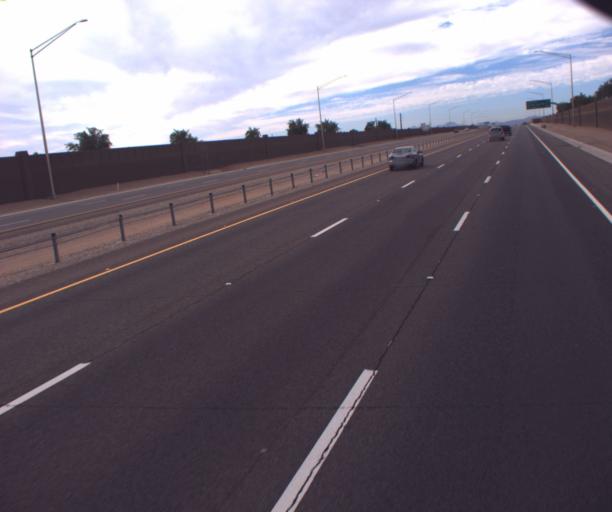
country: US
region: Arizona
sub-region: Maricopa County
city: Gilbert
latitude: 33.3285
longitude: -111.6995
